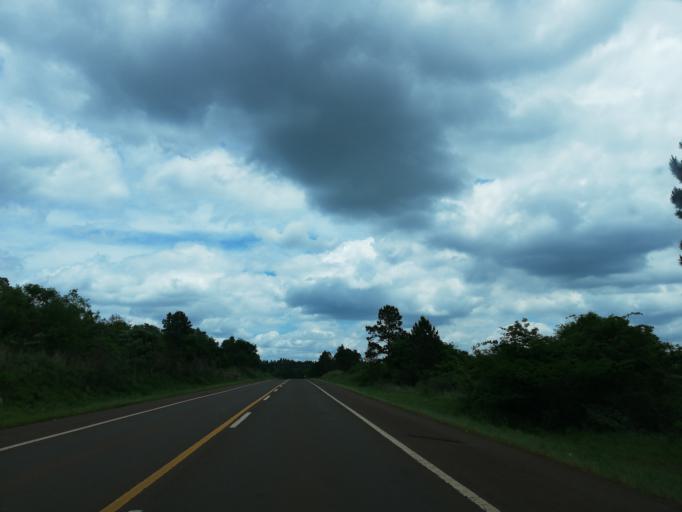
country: AR
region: Misiones
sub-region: Departamento de Leandro N. Alem
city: Leandro N. Alem
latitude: -27.6420
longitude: -55.3507
